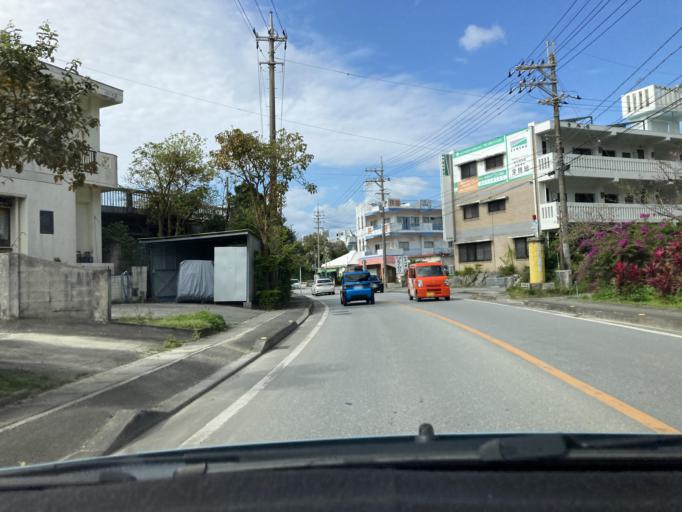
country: JP
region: Okinawa
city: Nago
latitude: 26.6575
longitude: 127.9030
